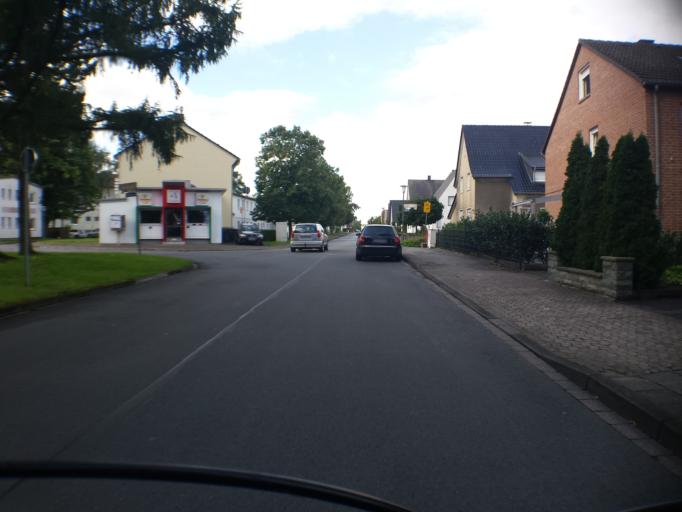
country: DE
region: North Rhine-Westphalia
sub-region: Regierungsbezirk Arnsberg
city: Lippstadt
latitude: 51.6795
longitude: 8.3050
